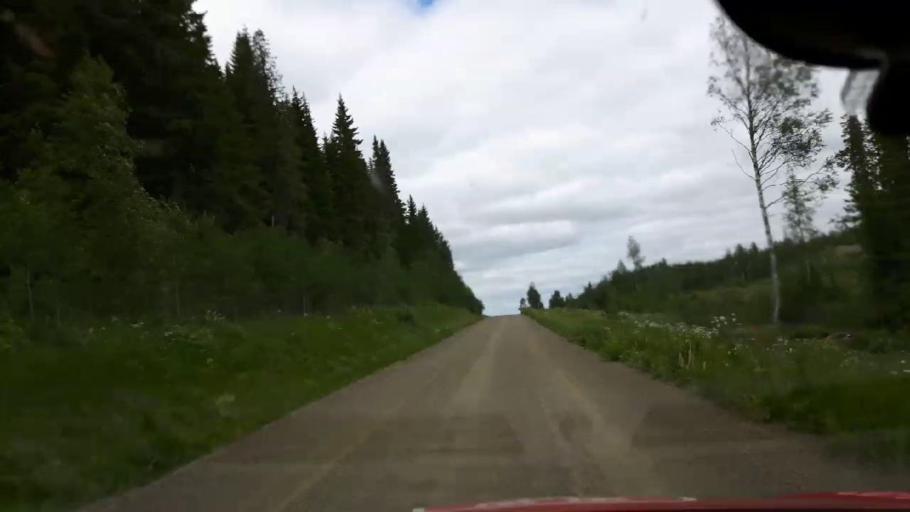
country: SE
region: Jaemtland
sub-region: OEstersunds Kommun
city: Brunflo
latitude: 62.9286
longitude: 15.0008
